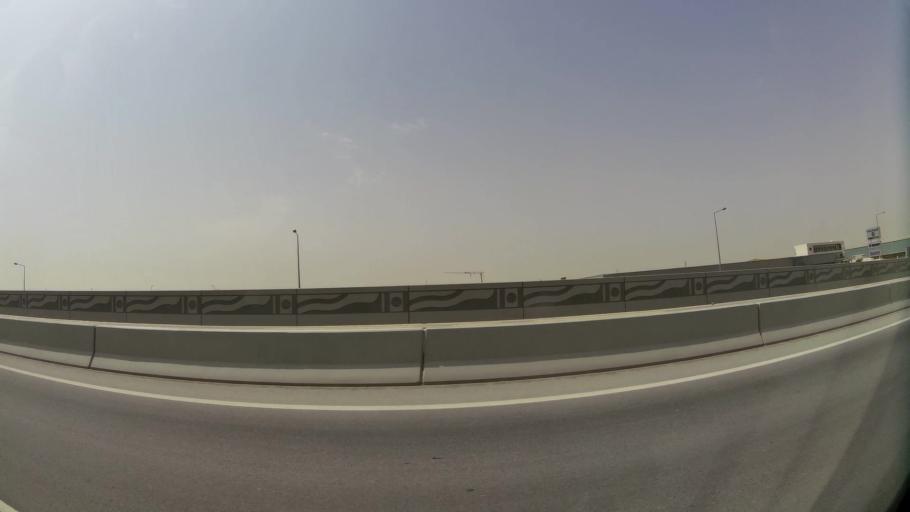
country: QA
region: Baladiyat ar Rayyan
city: Ar Rayyan
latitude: 25.2053
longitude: 51.4464
